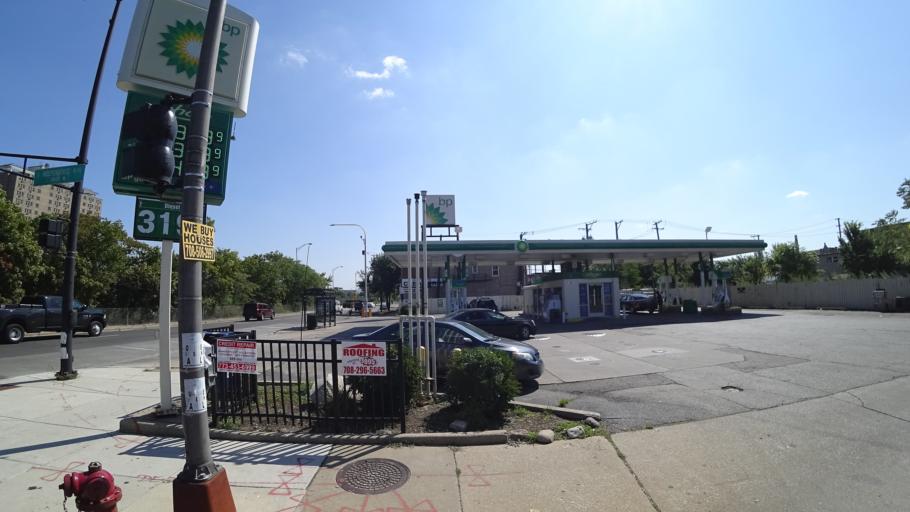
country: US
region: Illinois
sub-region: Cook County
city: Cicero
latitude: 41.8733
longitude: -87.7197
